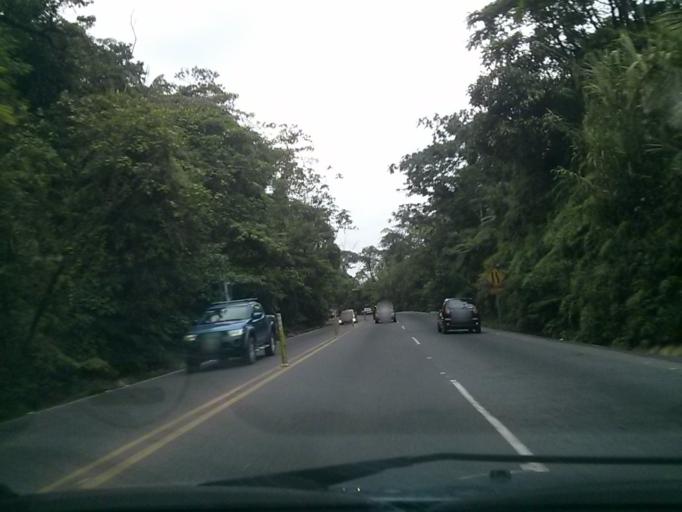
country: CR
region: San Jose
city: Dulce Nombre de Jesus
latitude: 10.1592
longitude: -83.9606
